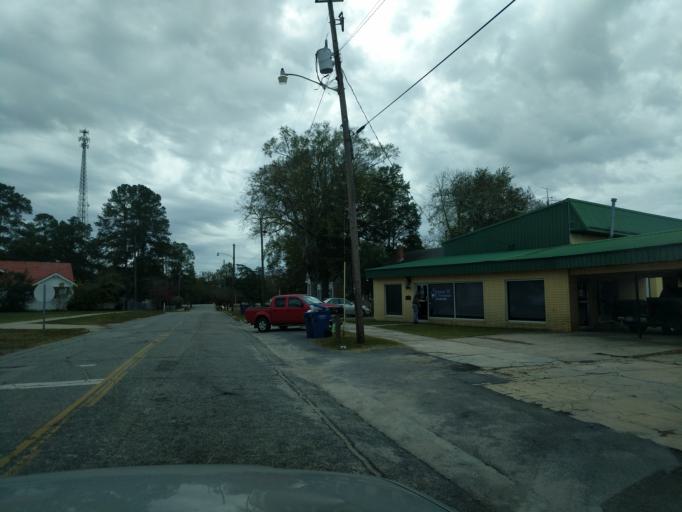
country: US
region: South Carolina
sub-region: Lexington County
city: Batesburg
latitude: 33.9061
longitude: -81.5480
